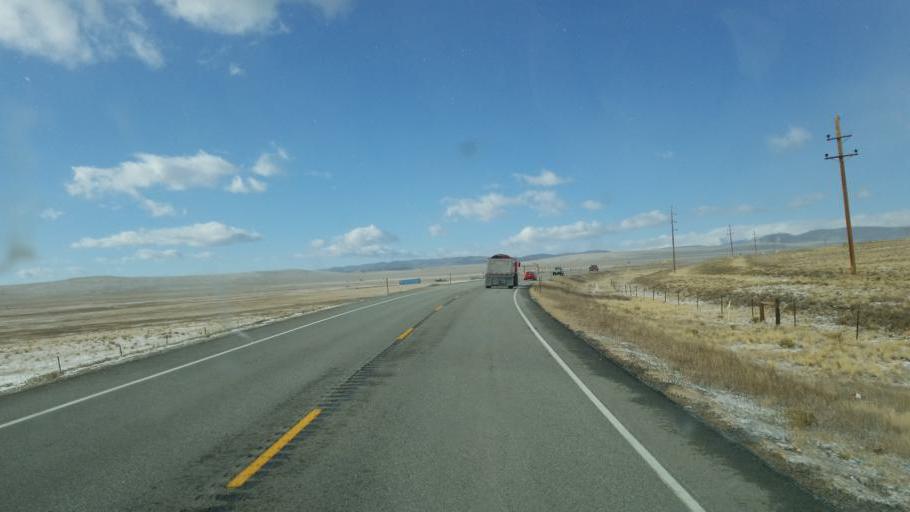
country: US
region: Colorado
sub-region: Park County
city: Fairplay
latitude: 39.3579
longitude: -105.8186
